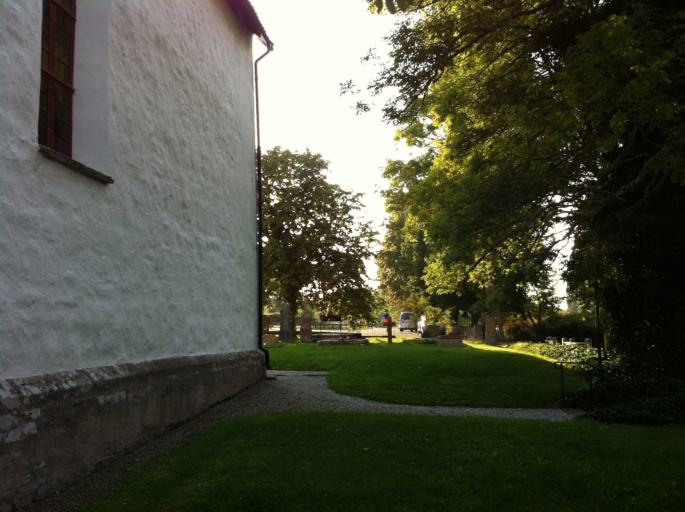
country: SE
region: Gotland
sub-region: Gotland
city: Slite
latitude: 57.4219
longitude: 18.8589
